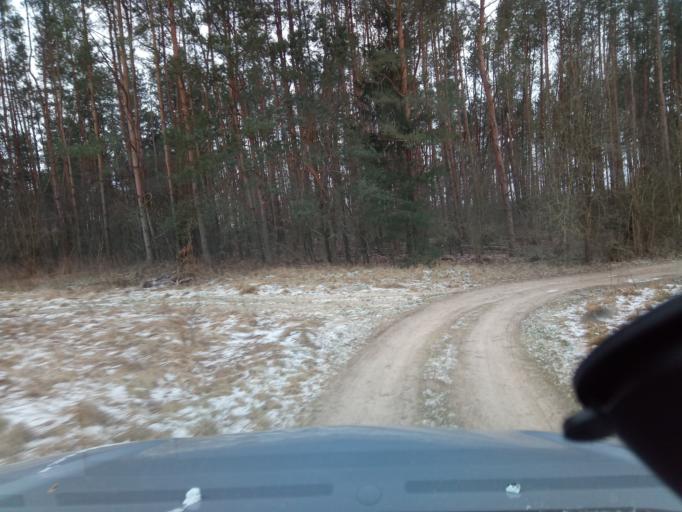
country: LT
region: Alytaus apskritis
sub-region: Alytaus rajonas
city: Daugai
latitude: 54.3755
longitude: 24.4289
